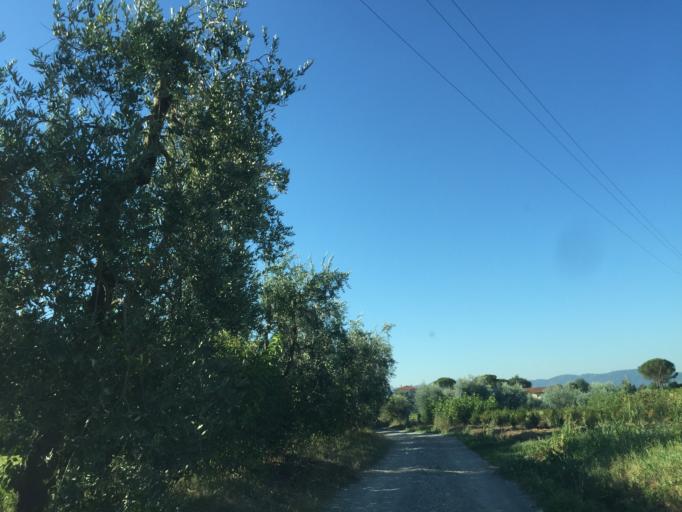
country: IT
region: Tuscany
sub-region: Provincia di Pistoia
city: Pistoia
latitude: 43.9449
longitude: 10.9401
